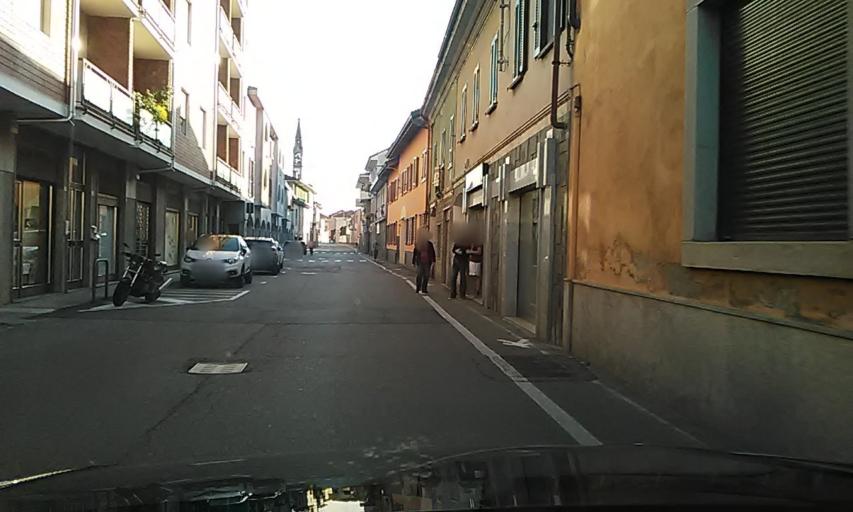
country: IT
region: Piedmont
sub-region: Provincia di Novara
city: Momo
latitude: 45.5737
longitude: 8.5555
